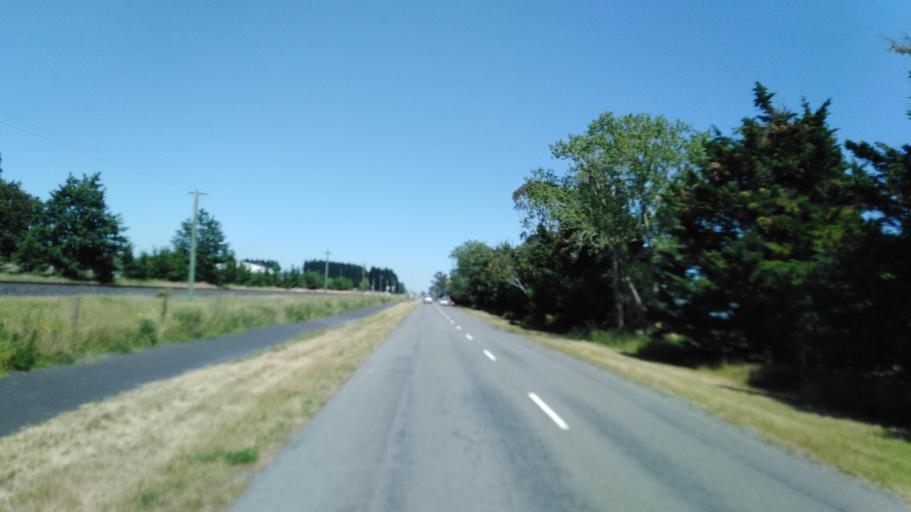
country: NZ
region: Canterbury
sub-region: Selwyn District
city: Prebbleton
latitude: -43.5590
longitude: 172.4611
